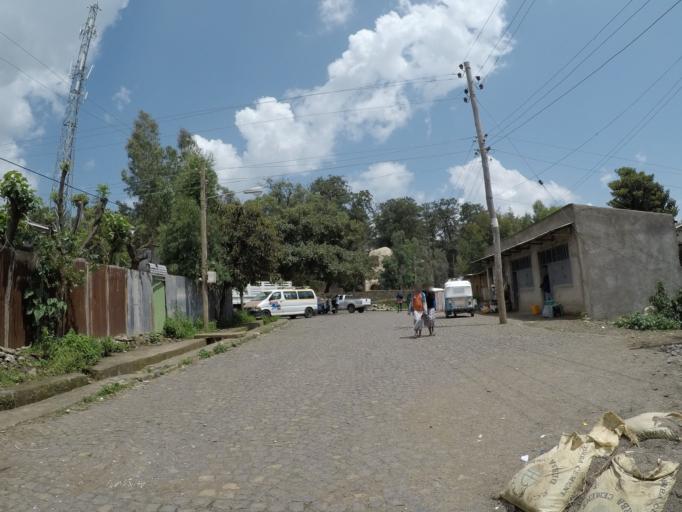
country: ET
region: Amhara
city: Gondar
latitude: 12.6130
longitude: 37.4795
